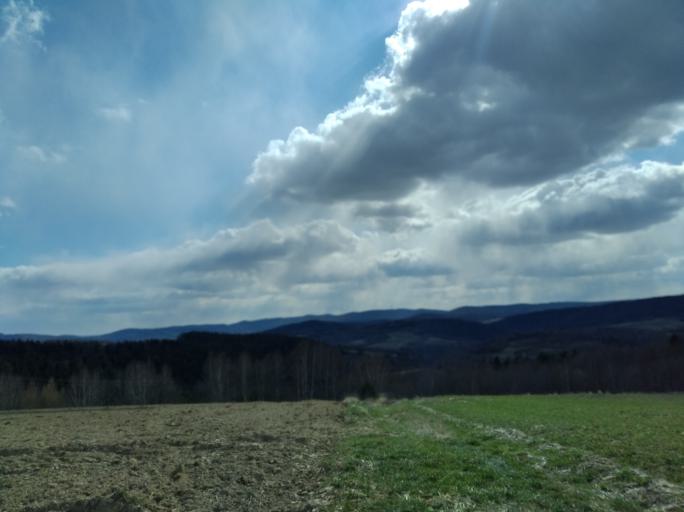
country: PL
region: Subcarpathian Voivodeship
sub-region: Powiat strzyzowski
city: Jawornik
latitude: 49.8384
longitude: 21.8539
